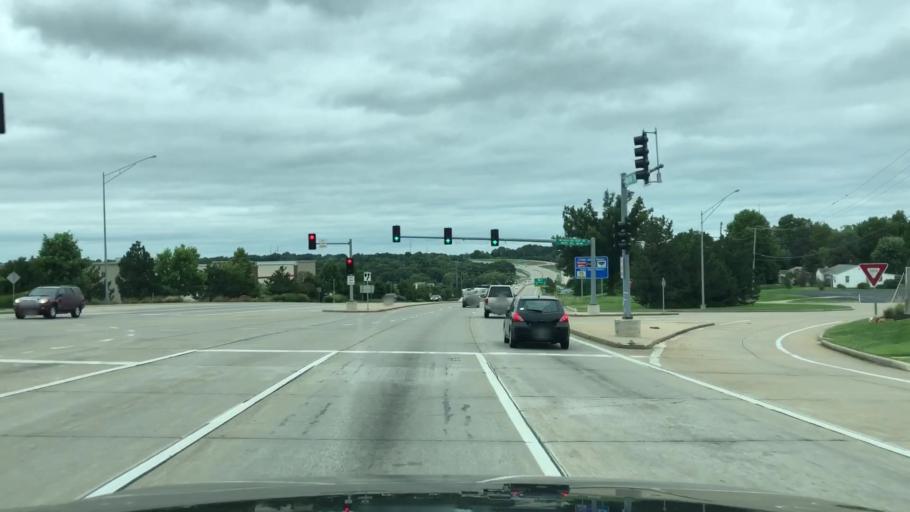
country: US
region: Missouri
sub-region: Saint Louis County
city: Manchester
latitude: 38.5993
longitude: -90.5089
